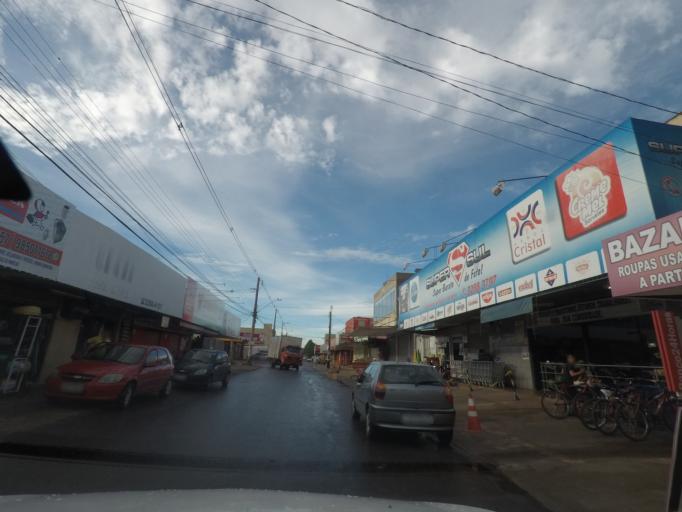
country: BR
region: Goias
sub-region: Aparecida De Goiania
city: Aparecida de Goiania
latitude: -16.7621
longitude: -49.3512
